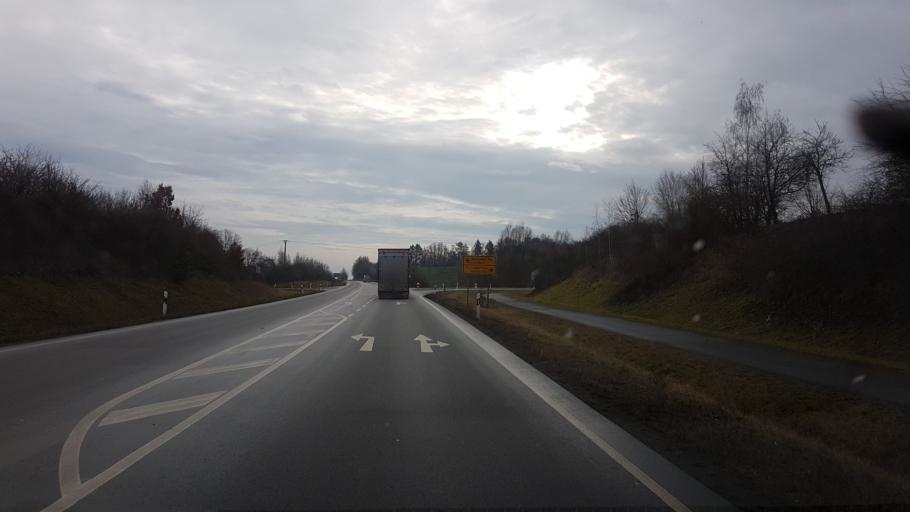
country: DE
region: Bavaria
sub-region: Upper Franconia
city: Reckendorf
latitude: 50.0346
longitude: 10.8248
